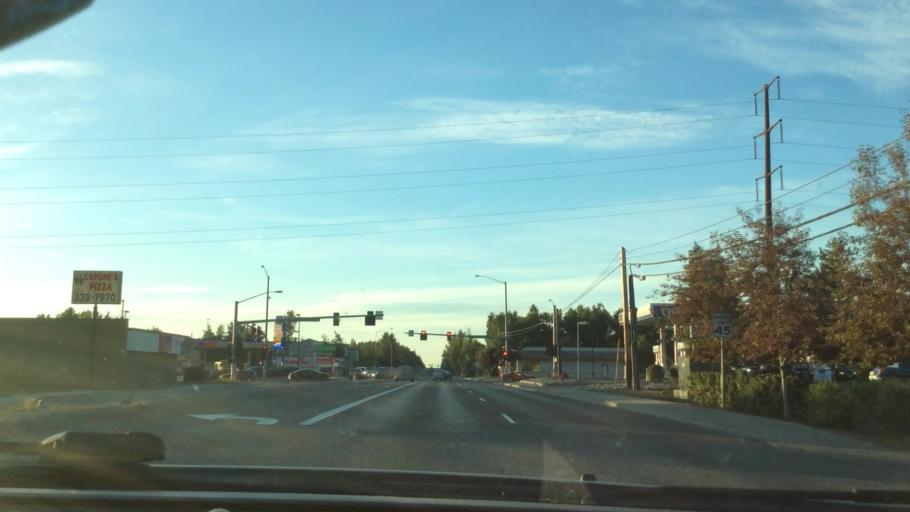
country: US
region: Alaska
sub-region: Anchorage Municipality
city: Anchorage
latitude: 61.1942
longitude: -149.7783
